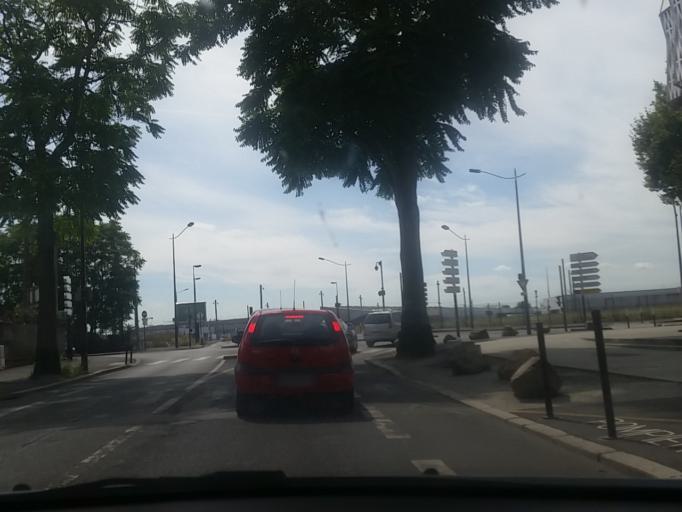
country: FR
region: Pays de la Loire
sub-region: Departement de la Loire-Atlantique
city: Nantes
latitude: 47.2048
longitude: -1.5630
